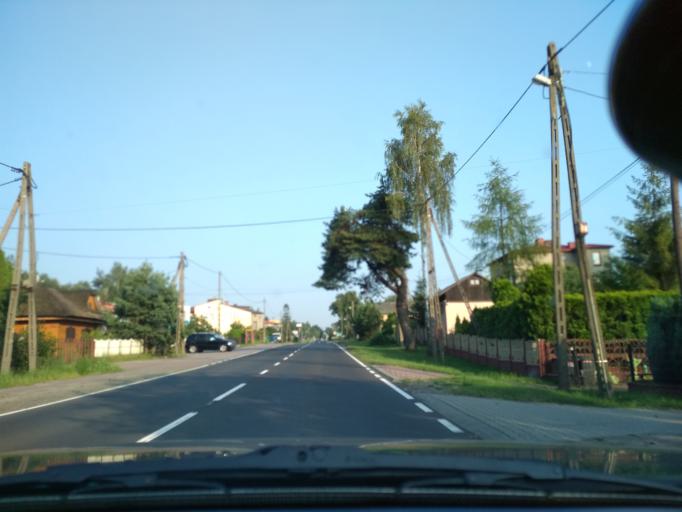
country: PL
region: Silesian Voivodeship
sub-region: Powiat zawiercianski
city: Ogrodzieniec
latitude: 50.4680
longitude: 19.4865
